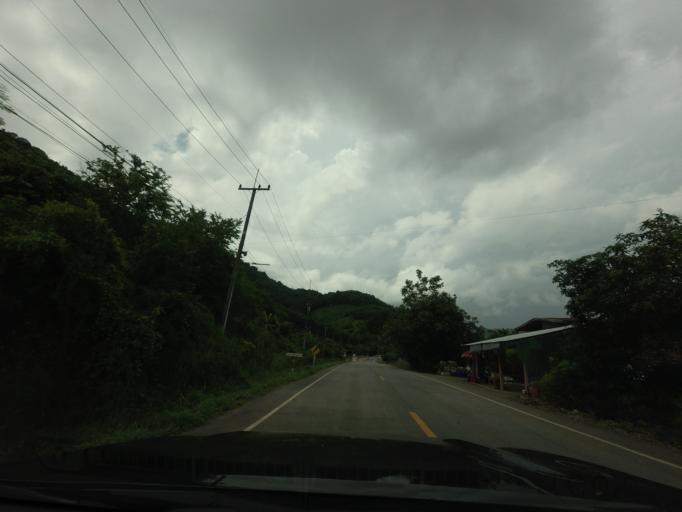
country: TH
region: Loei
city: Pak Chom
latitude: 18.0625
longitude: 101.7941
